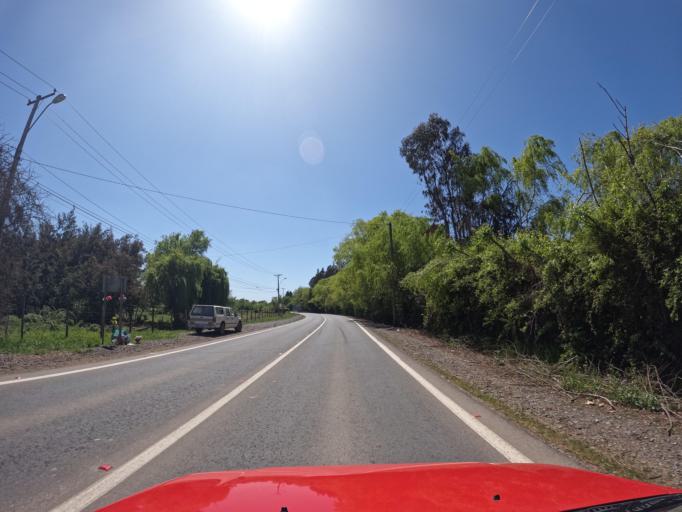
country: CL
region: Maule
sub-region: Provincia de Linares
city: Colbun
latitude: -35.7536
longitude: -71.4176
